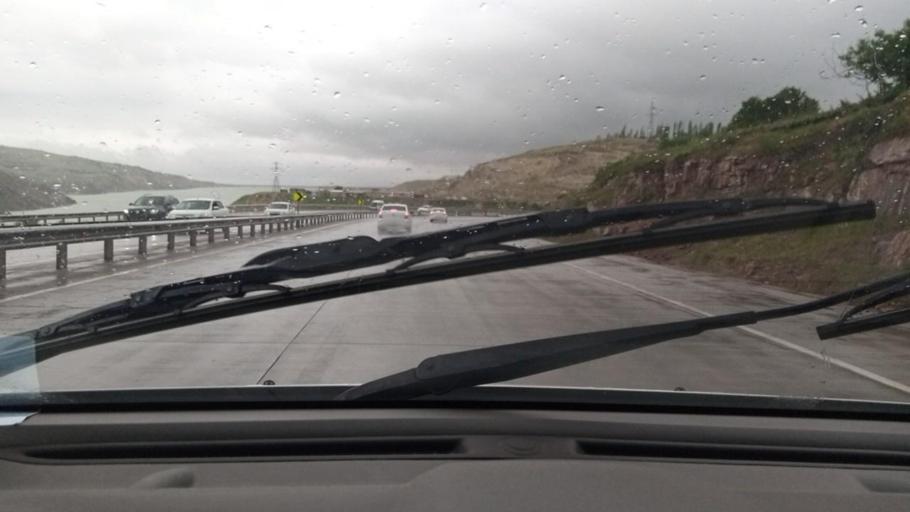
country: UZ
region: Toshkent
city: Angren
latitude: 41.0737
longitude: 70.2576
